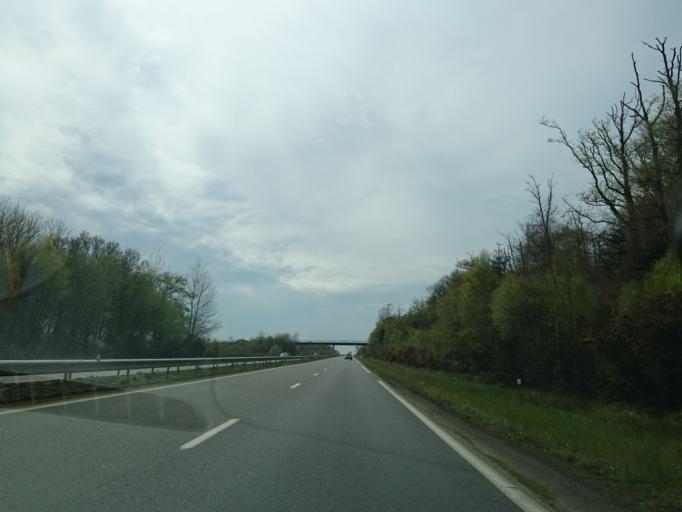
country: FR
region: Brittany
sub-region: Departement des Cotes-d'Armor
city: Plelan-le-Petit
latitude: 48.4237
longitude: -2.2490
